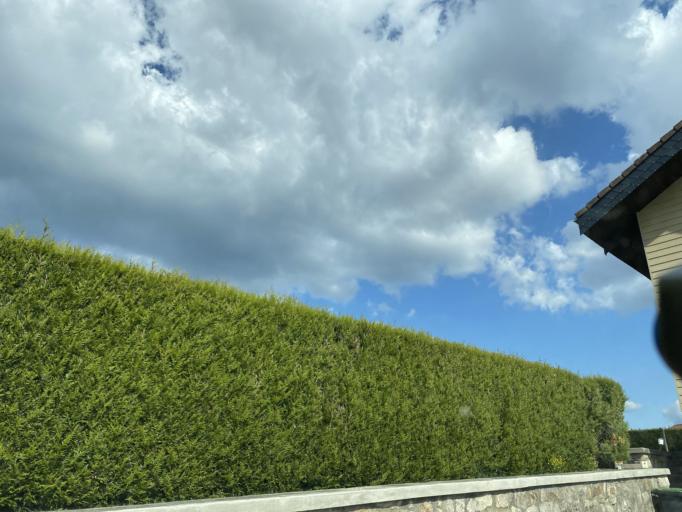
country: FR
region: Auvergne
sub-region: Departement du Puy-de-Dome
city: Celles-sur-Durolle
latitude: 45.7782
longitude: 3.6648
